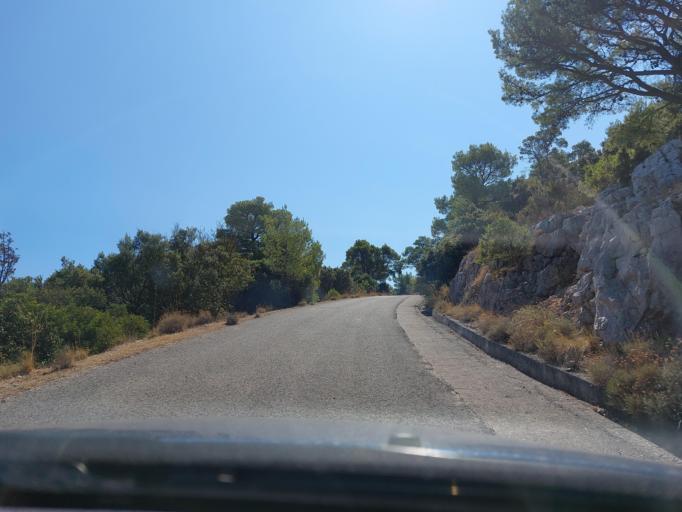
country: HR
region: Dubrovacko-Neretvanska
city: Smokvica
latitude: 42.7471
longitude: 16.8525
